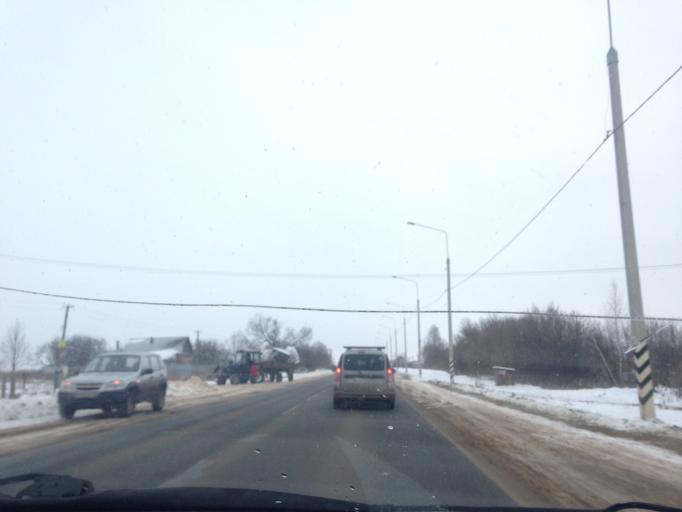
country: RU
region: Tula
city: Shchekino
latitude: 53.9835
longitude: 37.5032
